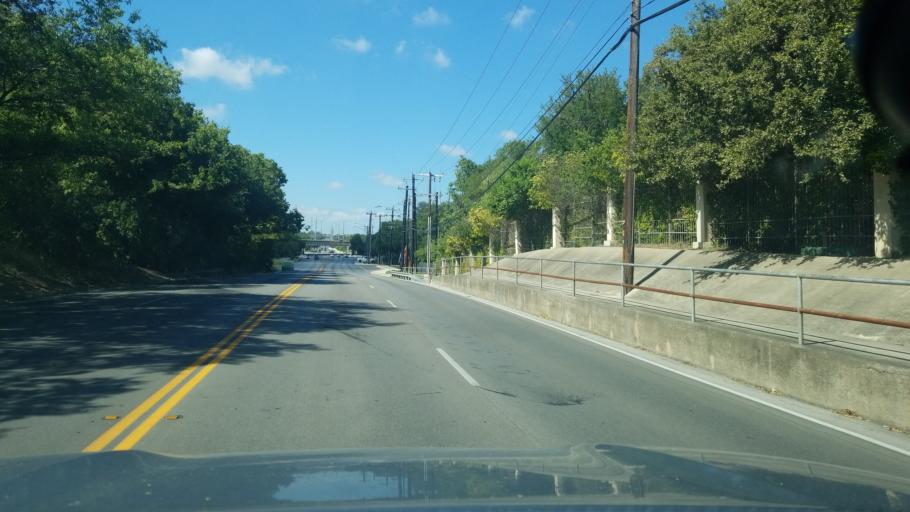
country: US
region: Texas
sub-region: Bexar County
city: Hollywood Park
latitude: 29.5609
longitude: -98.4943
